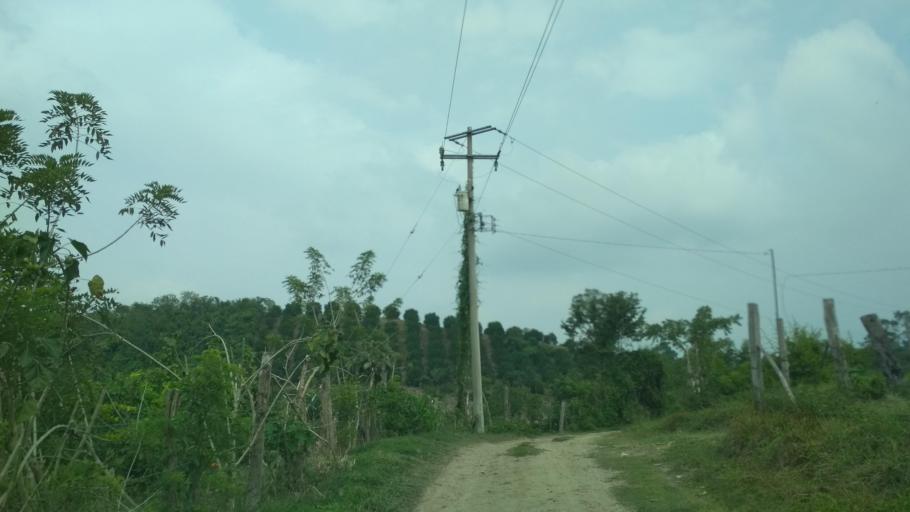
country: MM
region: Kayah
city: Loikaw
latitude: 20.2130
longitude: 97.3153
